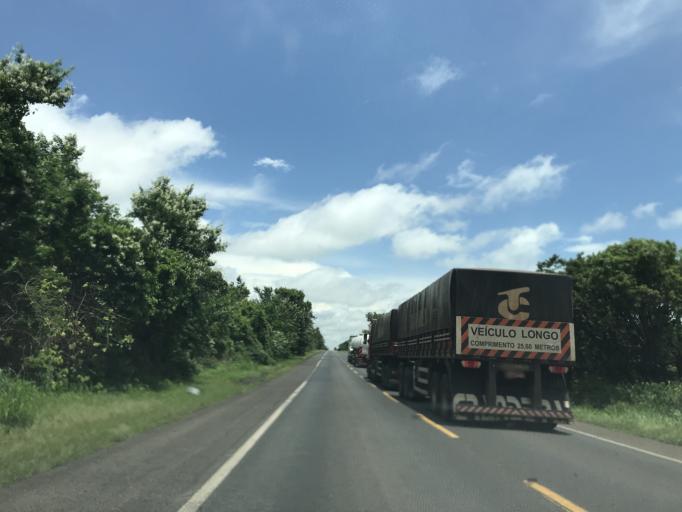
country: BR
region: Minas Gerais
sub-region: Prata
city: Prata
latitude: -19.6467
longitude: -48.9712
